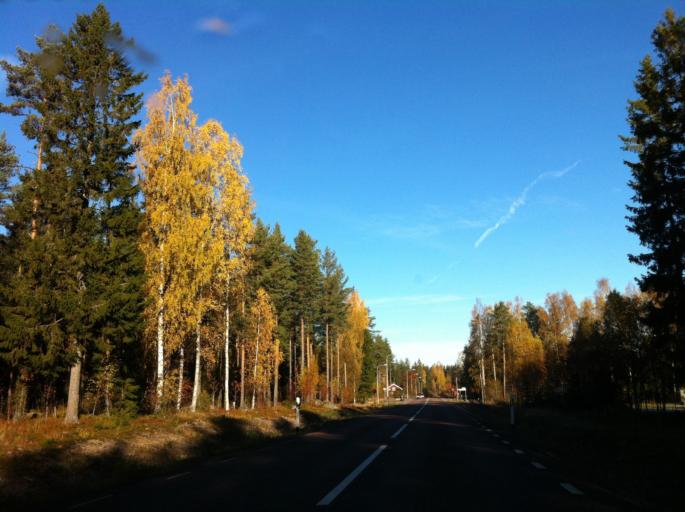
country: SE
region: Gaevleborg
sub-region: Gavle Kommun
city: Gavle
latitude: 60.5539
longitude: 17.1240
